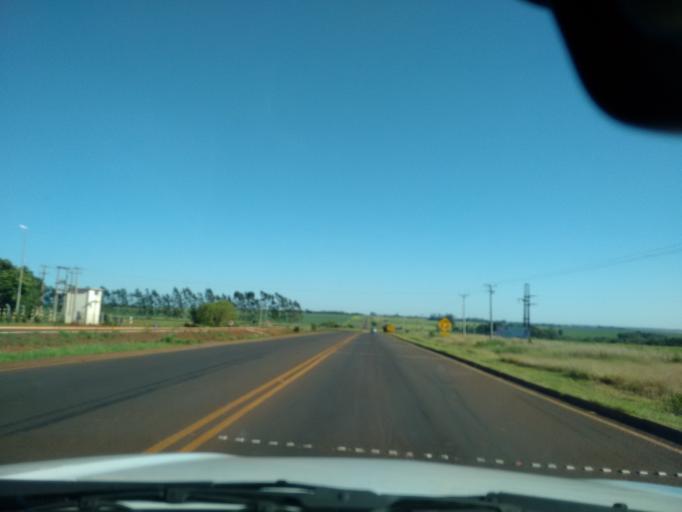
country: BR
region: Mato Grosso do Sul
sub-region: Dourados
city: Dourados
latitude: -22.3226
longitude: -54.8192
